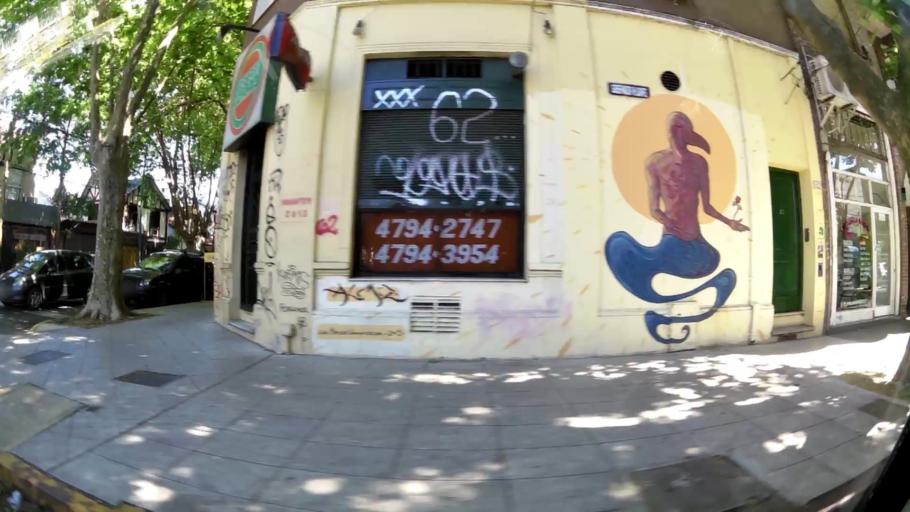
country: AR
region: Buenos Aires
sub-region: Partido de Vicente Lopez
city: Olivos
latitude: -34.5148
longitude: -58.4930
